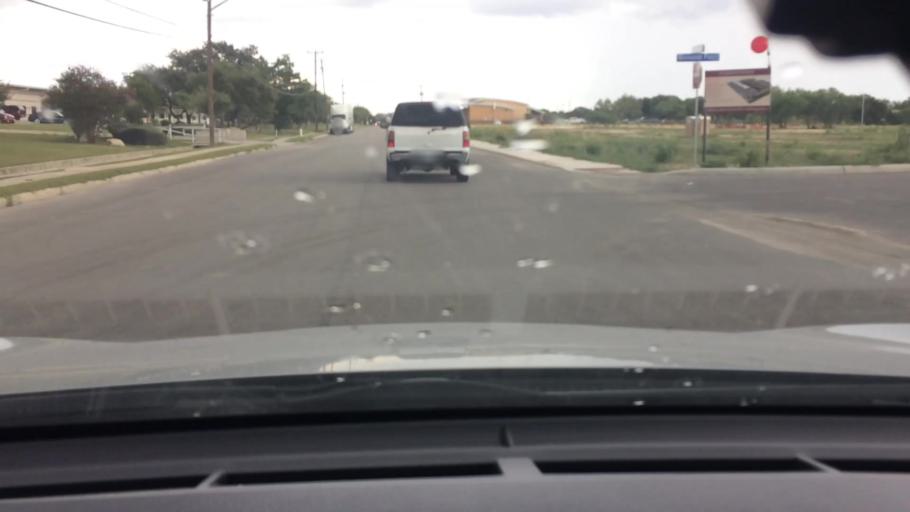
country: US
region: Texas
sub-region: Bexar County
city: Shavano Park
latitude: 29.5730
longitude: -98.5904
